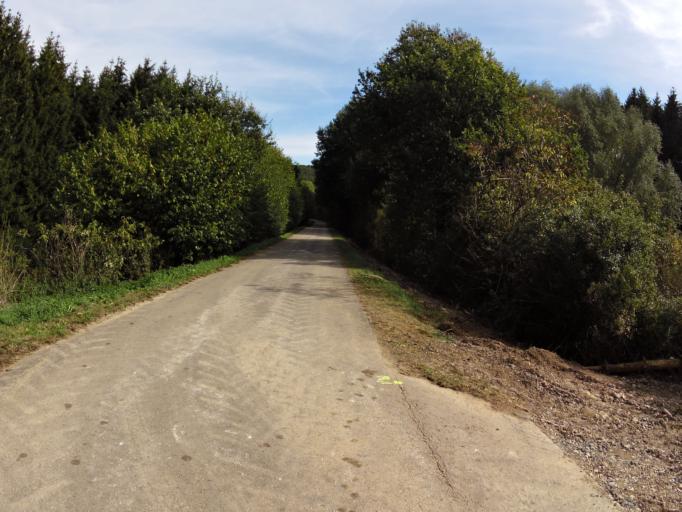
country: DE
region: Rheinland-Pfalz
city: Euscheid
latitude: 50.1258
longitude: 6.2942
